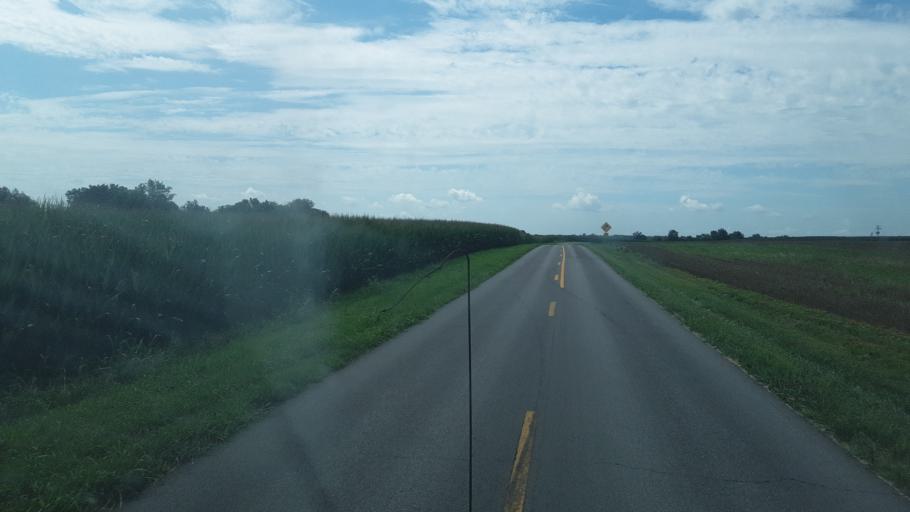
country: US
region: Kentucky
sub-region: Christian County
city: Oak Grove
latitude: 36.7471
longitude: -87.3172
